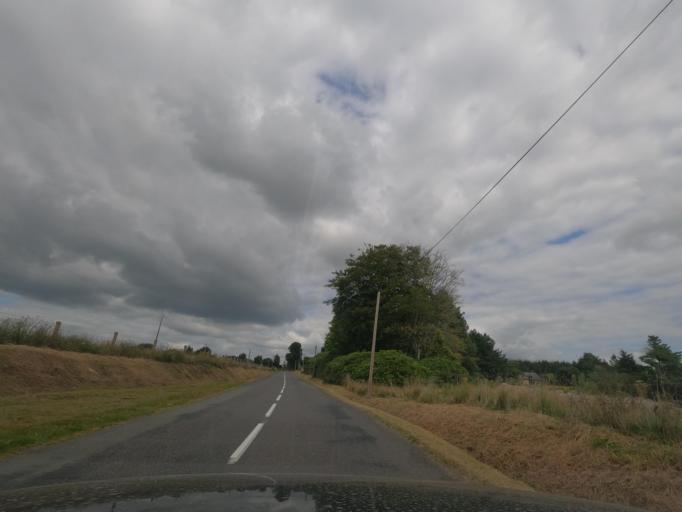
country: FR
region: Lower Normandy
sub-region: Departement de la Manche
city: Le Teilleul
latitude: 48.5038
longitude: -0.9121
